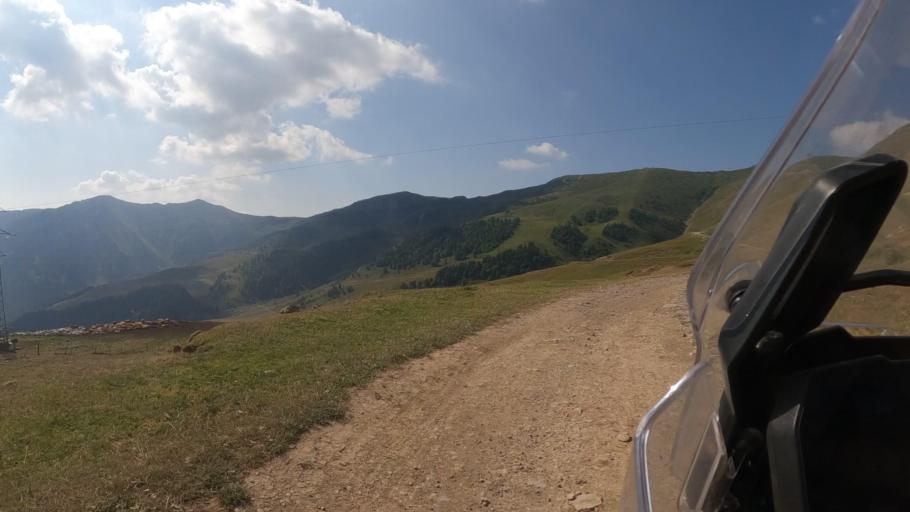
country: IT
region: Piedmont
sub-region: Provincia di Cuneo
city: Briga Alta
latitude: 44.0778
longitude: 7.7222
